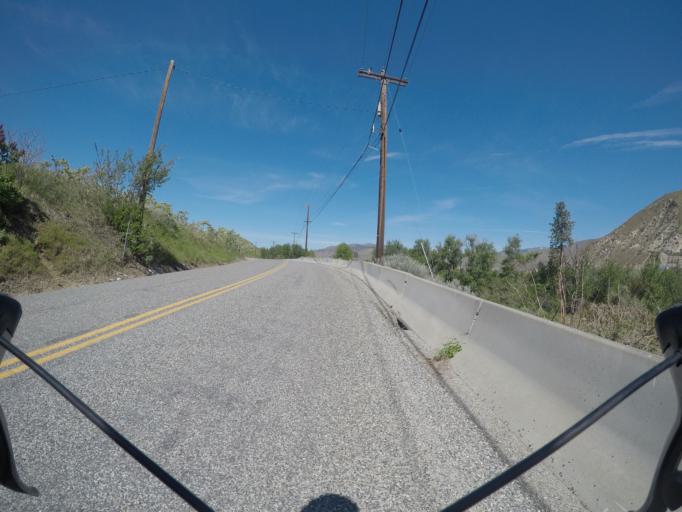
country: US
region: Washington
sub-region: Chelan County
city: Cashmere
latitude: 47.4891
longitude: -120.4211
